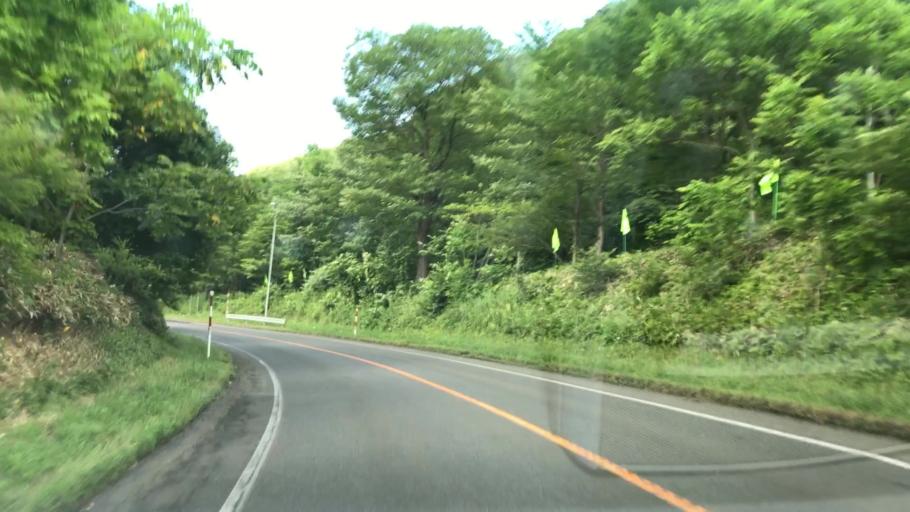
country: JP
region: Hokkaido
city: Shizunai-furukawacho
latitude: 42.8157
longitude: 142.4215
